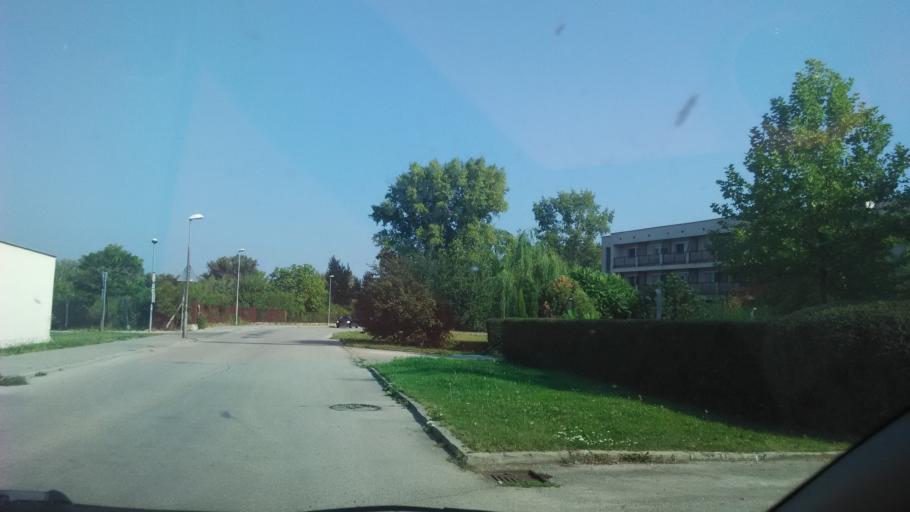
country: SK
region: Trnavsky
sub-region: Okres Trnava
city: Piestany
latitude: 48.5714
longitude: 17.8206
